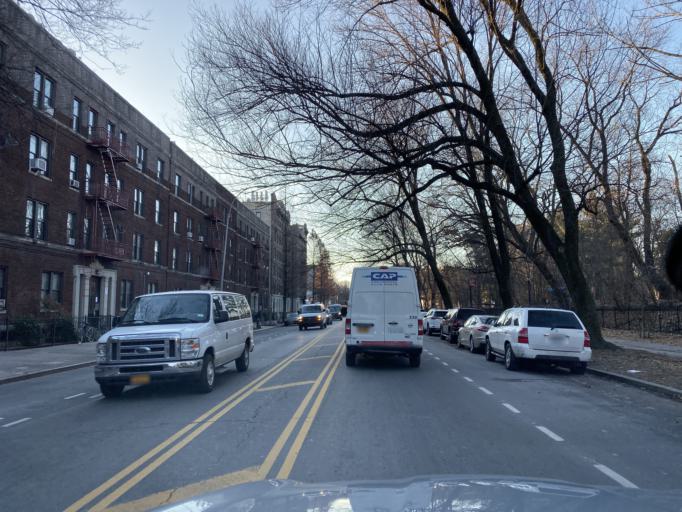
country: US
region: New York
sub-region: Kings County
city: Brooklyn
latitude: 40.6566
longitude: -73.9622
